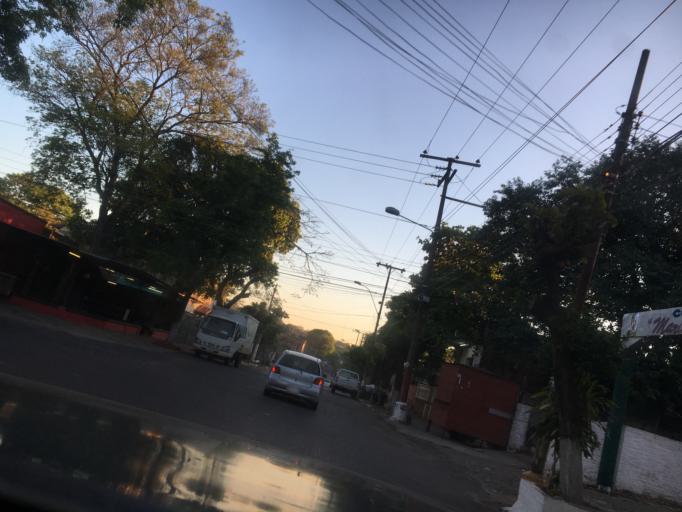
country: PY
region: Central
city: Lambare
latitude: -25.3198
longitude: -57.6101
